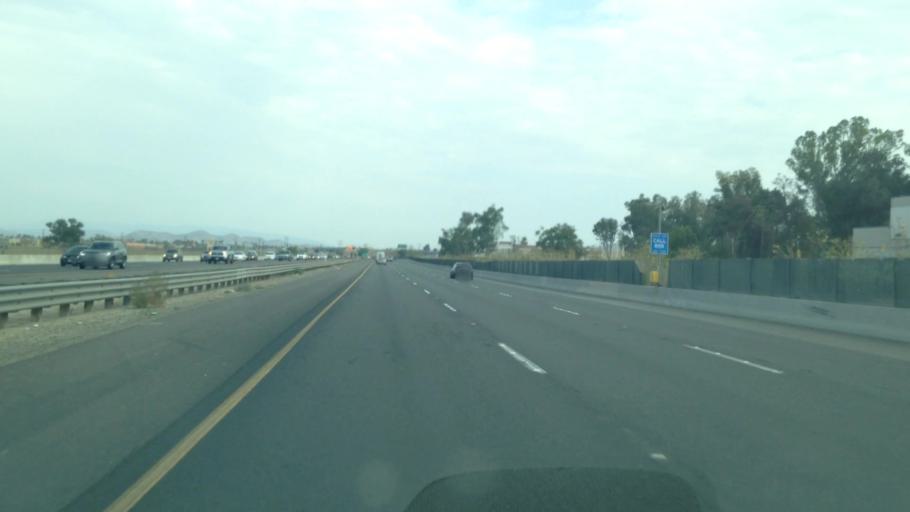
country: US
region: California
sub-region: Riverside County
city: Perris
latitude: 33.8159
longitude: -117.2394
